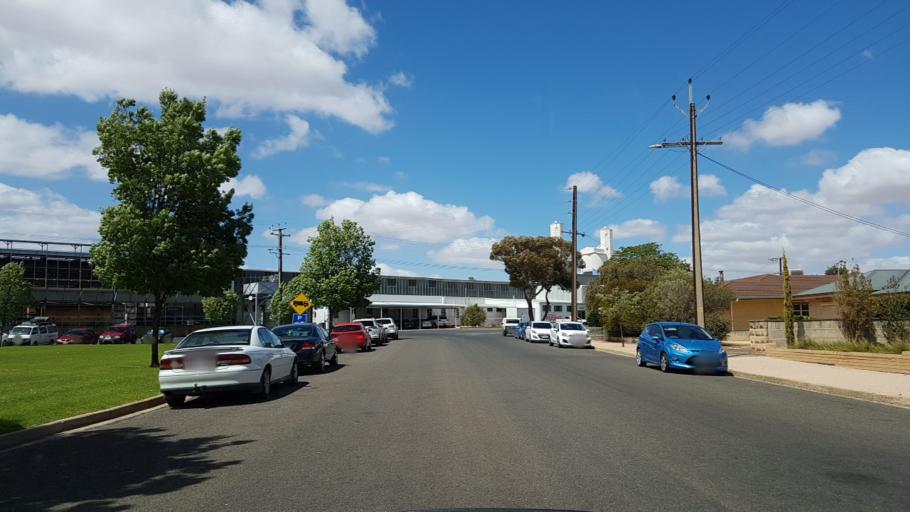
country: AU
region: South Australia
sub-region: Loxton Waikerie
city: Waikerie
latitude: -34.1825
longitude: 139.9880
